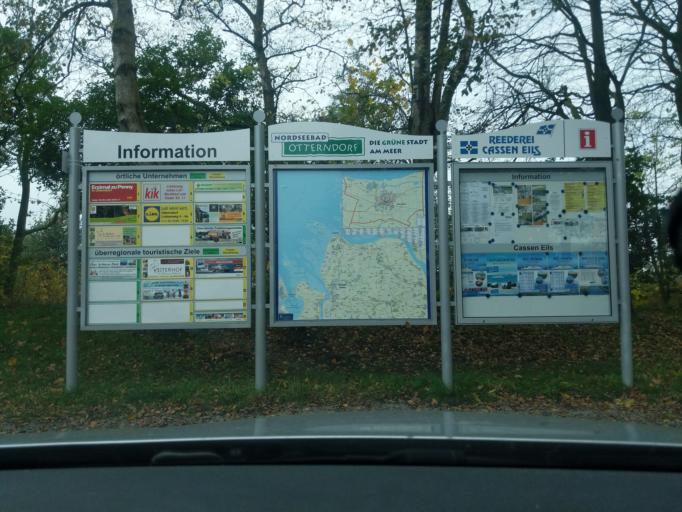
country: DE
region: Lower Saxony
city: Otterndorf
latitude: 53.8231
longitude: 8.8811
